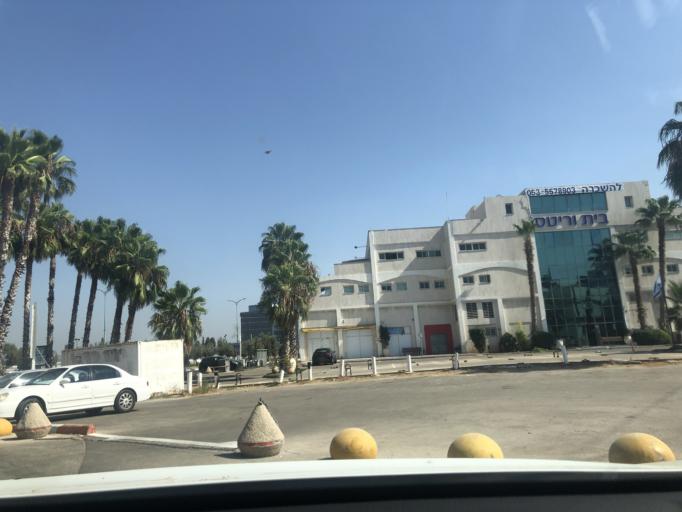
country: IL
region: Central District
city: Lod
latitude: 31.9669
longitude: 34.8999
